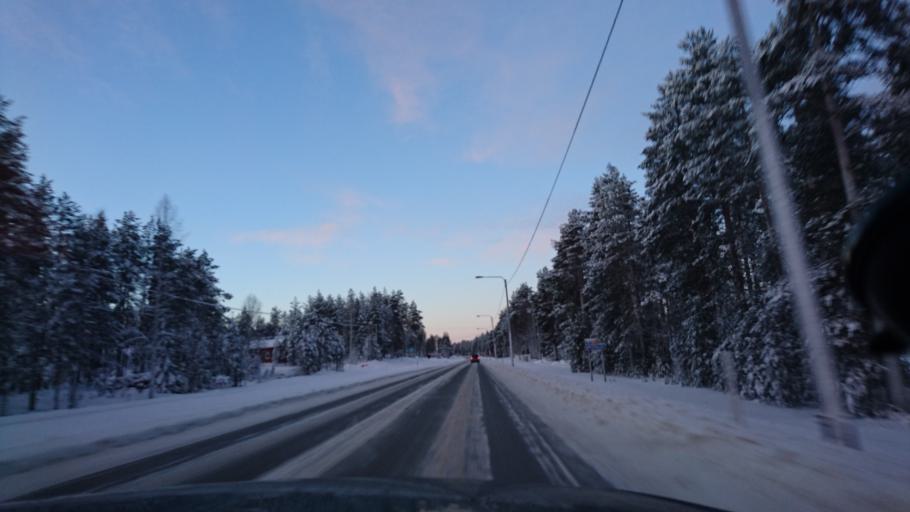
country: FI
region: Lapland
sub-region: Rovaniemi
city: Ranua
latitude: 65.9412
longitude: 26.4781
